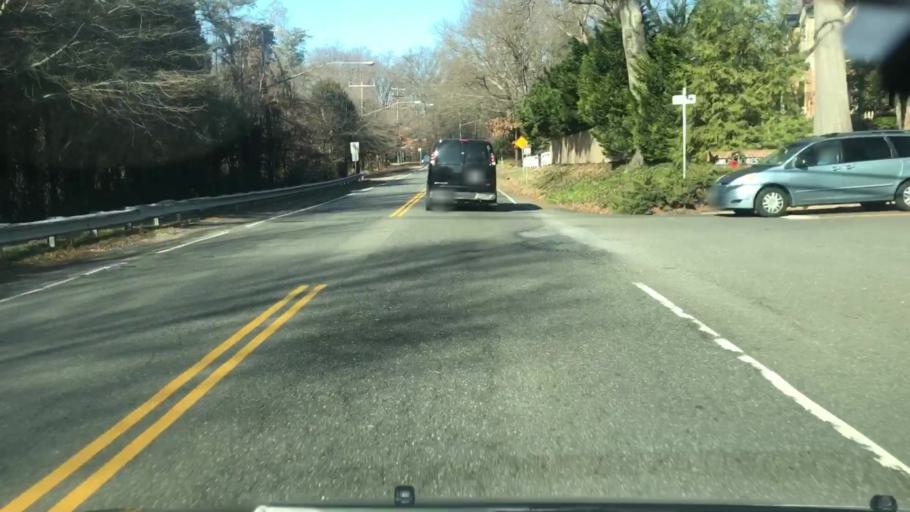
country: US
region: Virginia
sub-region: Fairfax County
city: Fort Hunt
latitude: 38.7590
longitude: -77.0586
